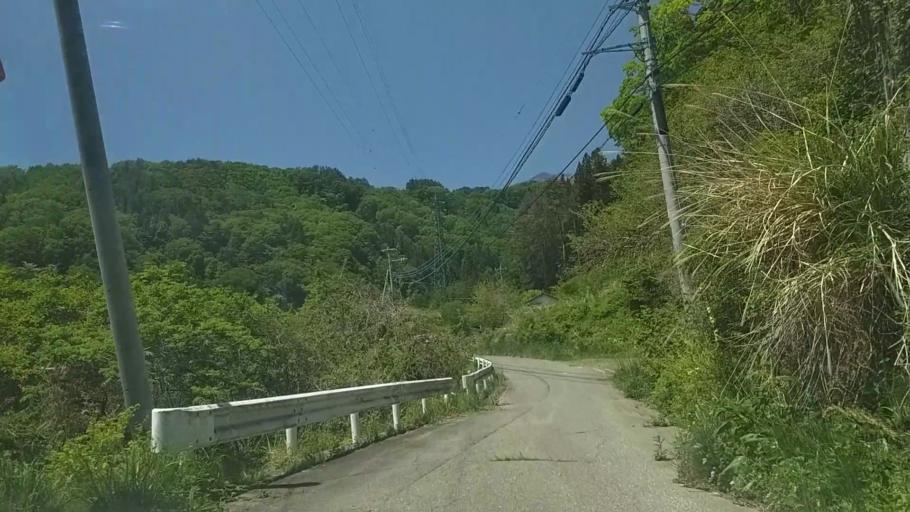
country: JP
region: Yamanashi
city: Nirasaki
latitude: 35.8761
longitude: 138.4319
